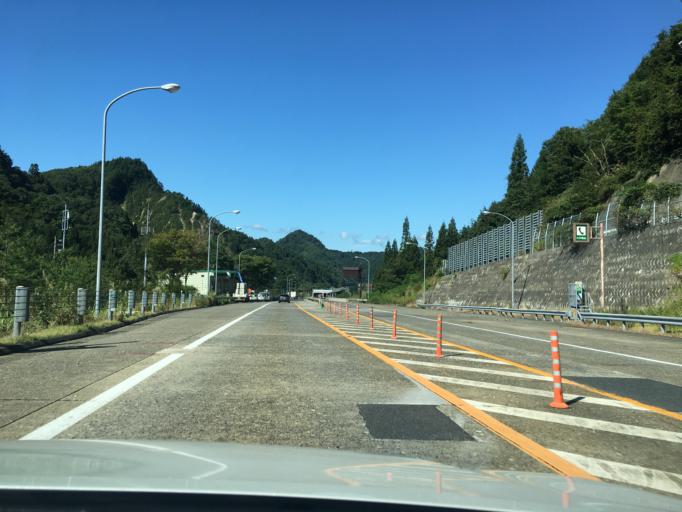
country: JP
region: Fukushima
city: Kitakata
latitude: 37.6048
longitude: 139.5428
